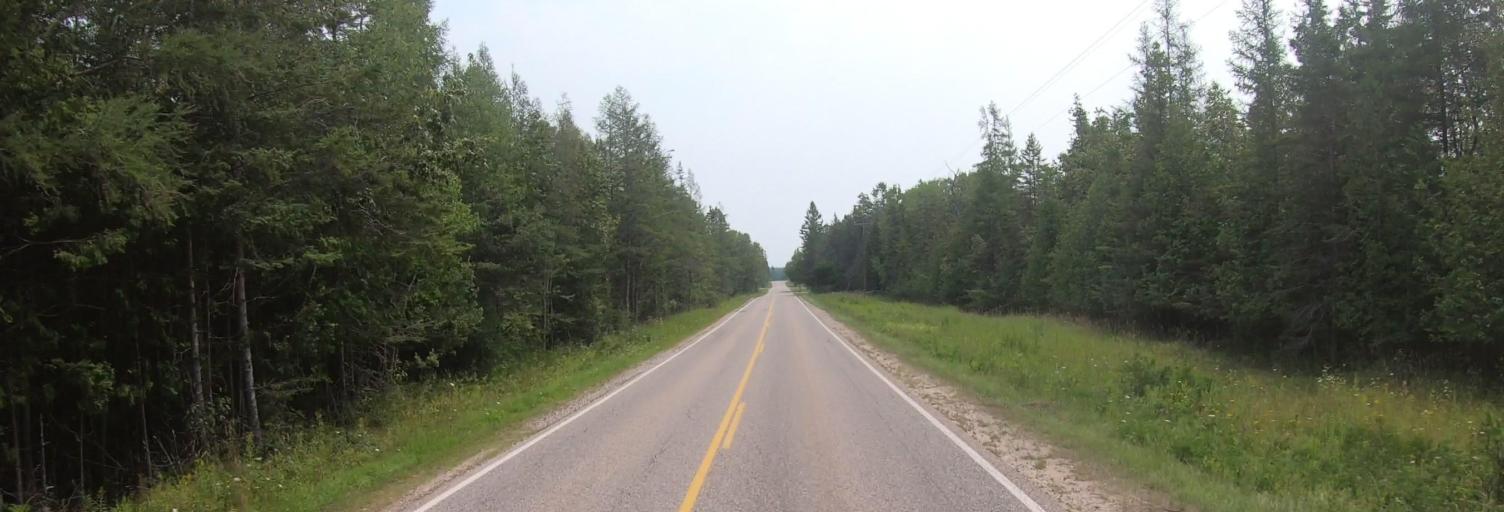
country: CA
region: Ontario
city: Thessalon
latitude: 45.9756
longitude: -83.6616
